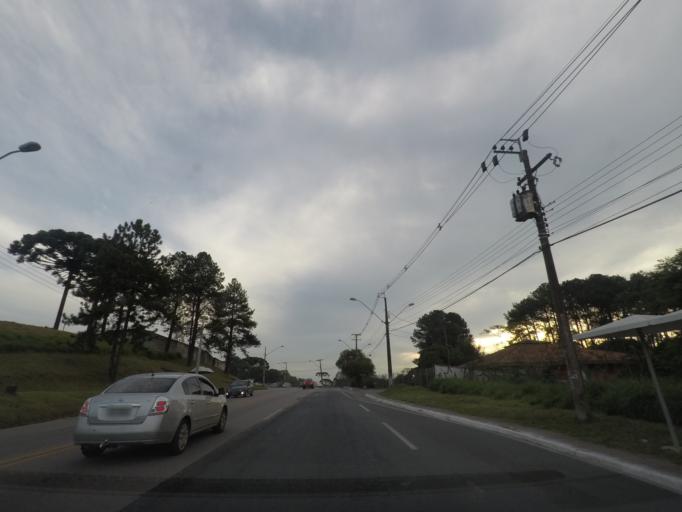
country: BR
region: Parana
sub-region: Curitiba
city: Curitiba
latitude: -25.3732
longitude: -49.2217
